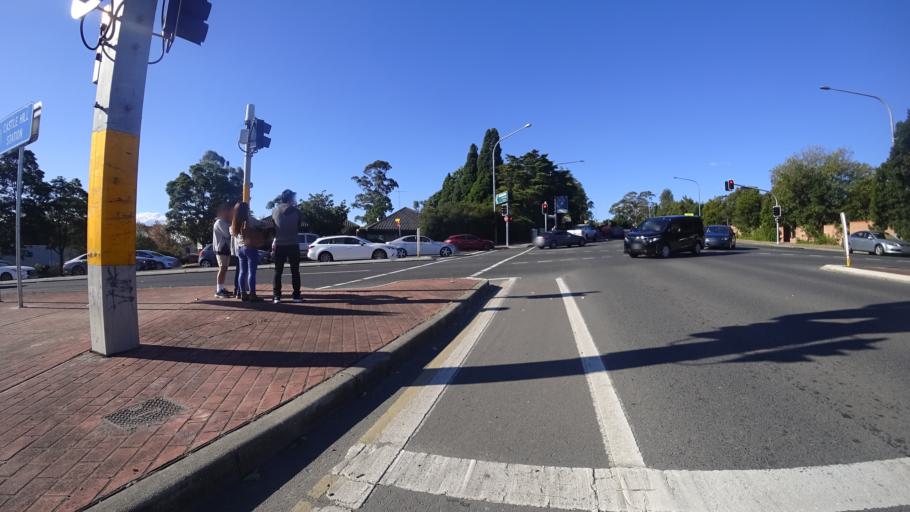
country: AU
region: New South Wales
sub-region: The Hills Shire
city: Castle Hill
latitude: -33.7312
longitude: 151.0097
